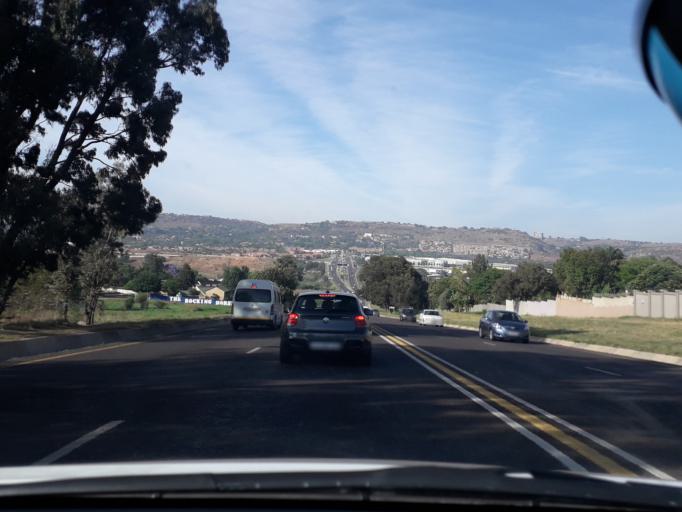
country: ZA
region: Gauteng
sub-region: City of Johannesburg Metropolitan Municipality
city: Roodepoort
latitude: -26.1165
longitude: 27.9161
